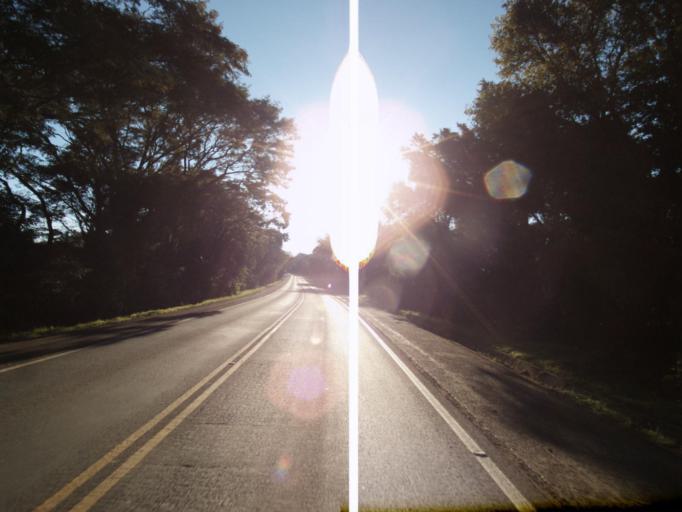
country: BR
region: Santa Catarina
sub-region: Chapeco
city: Chapeco
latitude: -26.9002
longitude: -52.8709
